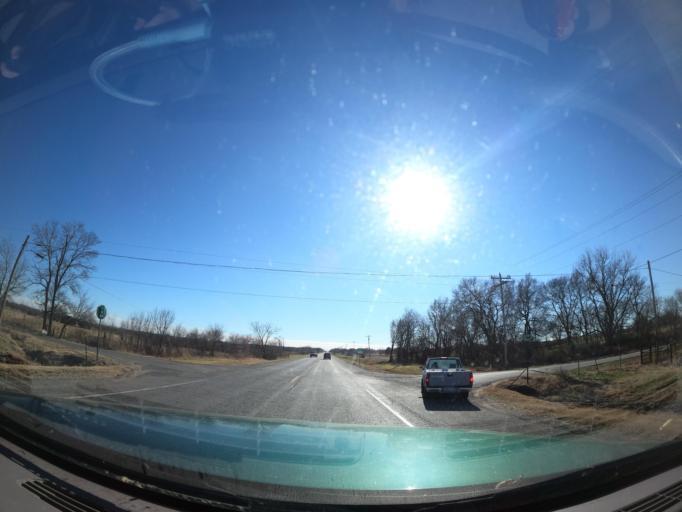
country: US
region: Oklahoma
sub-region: Muskogee County
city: Haskell
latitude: 35.8566
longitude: -95.6775
